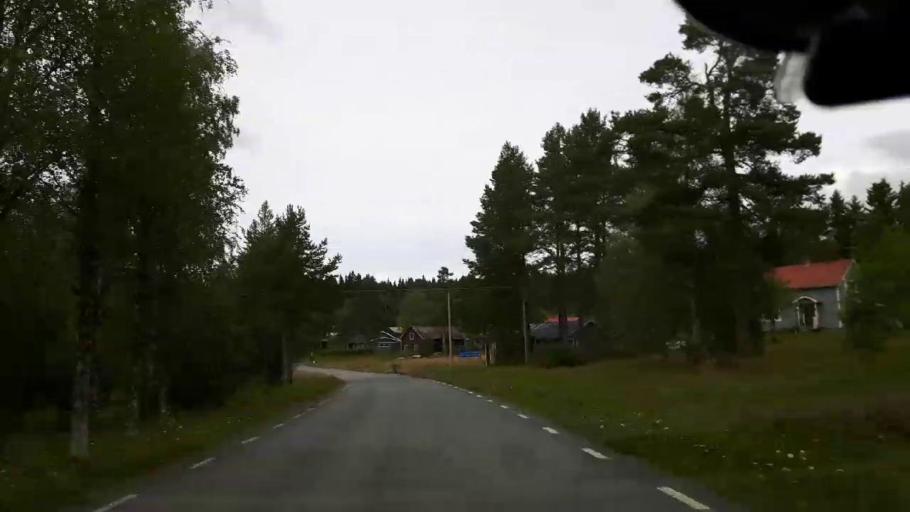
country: SE
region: Jaemtland
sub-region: Krokoms Kommun
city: Valla
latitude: 63.4729
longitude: 14.0666
